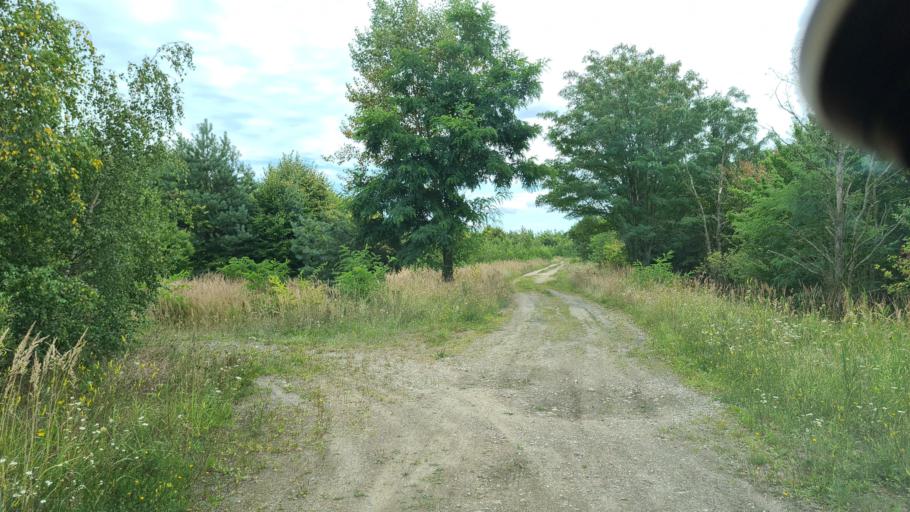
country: DE
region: Brandenburg
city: Spremberg
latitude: 51.5822
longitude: 14.3076
